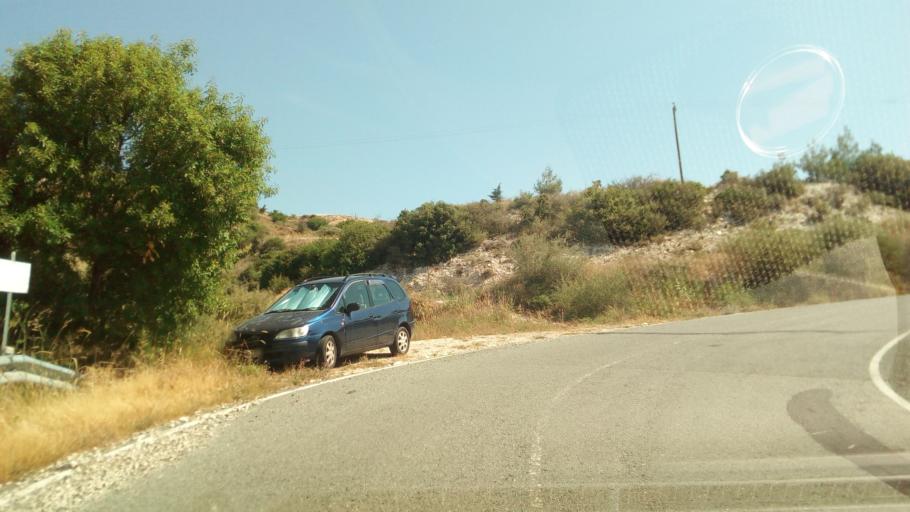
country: CY
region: Limassol
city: Pachna
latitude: 34.7927
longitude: 32.6917
